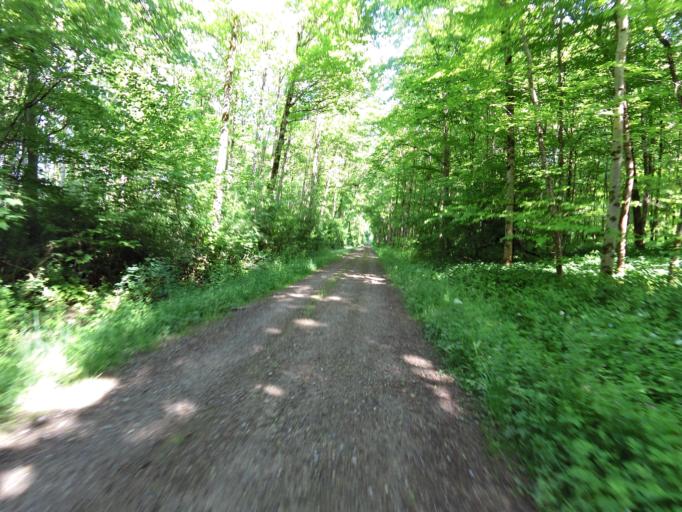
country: CH
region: Thurgau
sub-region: Frauenfeld District
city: Mullheim
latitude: 47.5876
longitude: 9.0019
